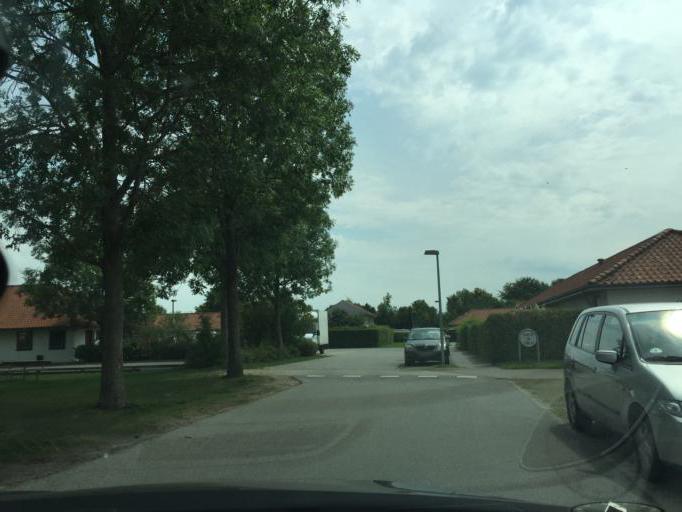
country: DK
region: South Denmark
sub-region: Odense Kommune
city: Neder Holluf
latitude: 55.3631
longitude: 10.4417
